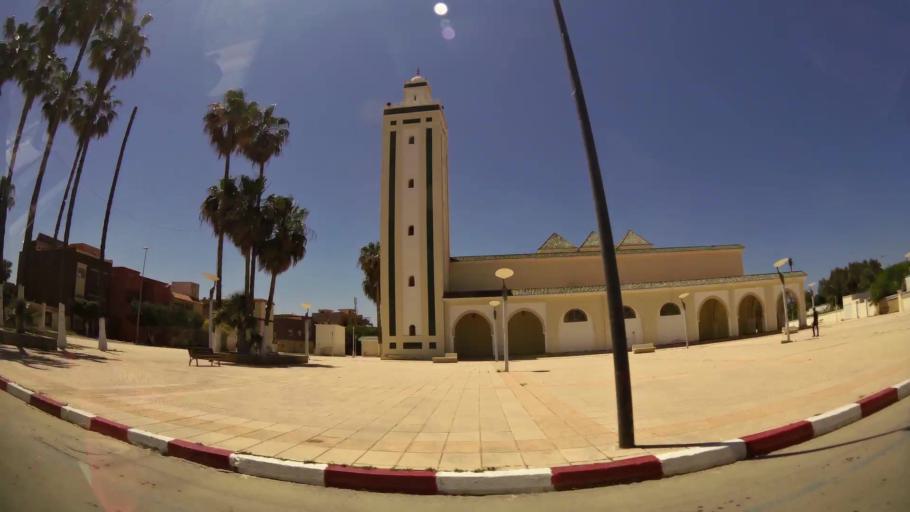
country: MA
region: Oriental
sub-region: Berkane-Taourirt
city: Madagh
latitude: 35.0796
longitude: -2.2158
